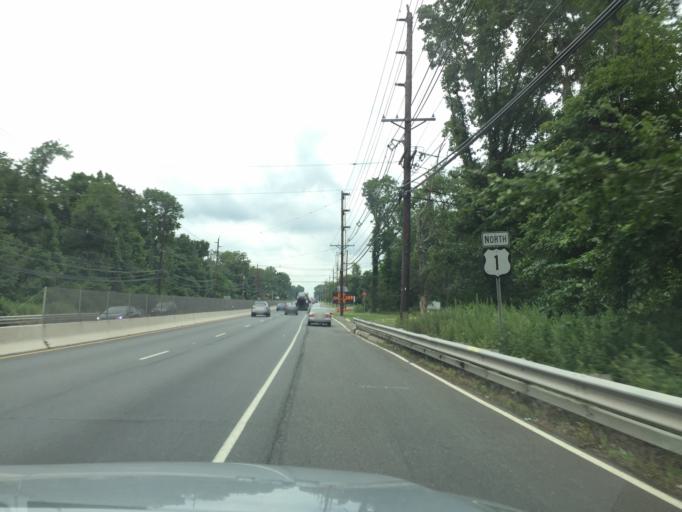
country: US
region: New Jersey
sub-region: Middlesex County
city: Heathcote
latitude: 40.3803
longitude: -74.5787
